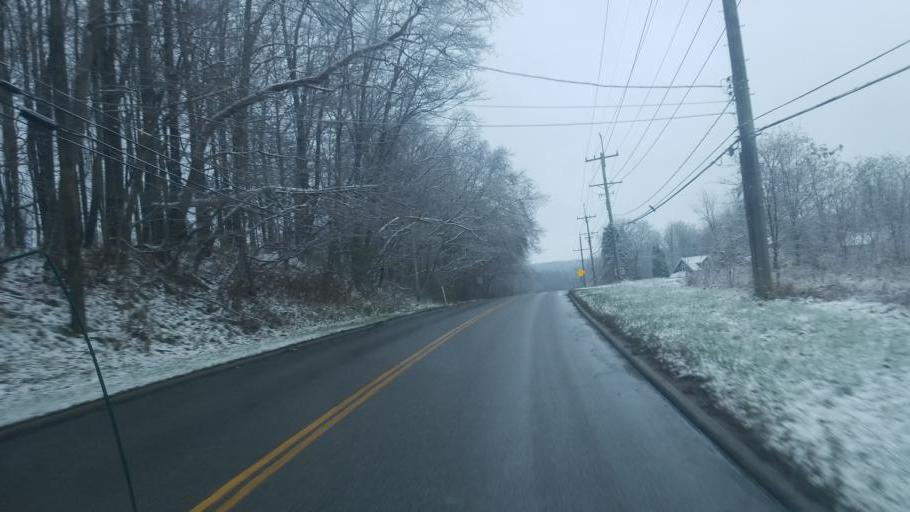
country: US
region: Ohio
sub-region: Geauga County
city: Burton
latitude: 41.4704
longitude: -81.1350
